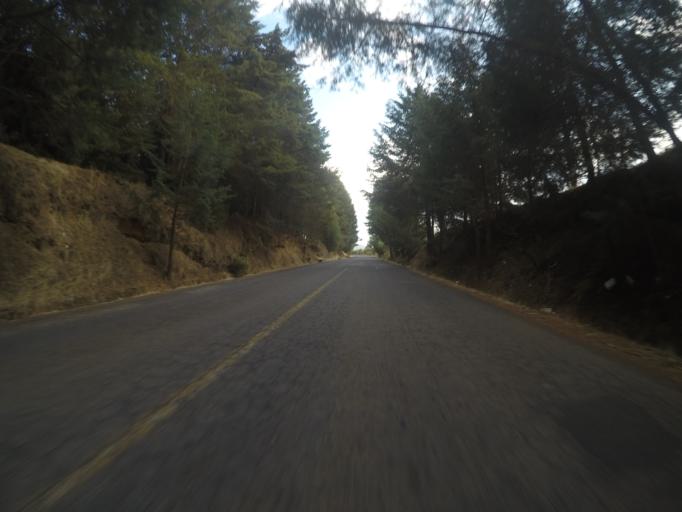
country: MX
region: Mexico
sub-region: Xalatlaco
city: San Juan Tomasquillo Herradura
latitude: 19.1639
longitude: -99.3909
